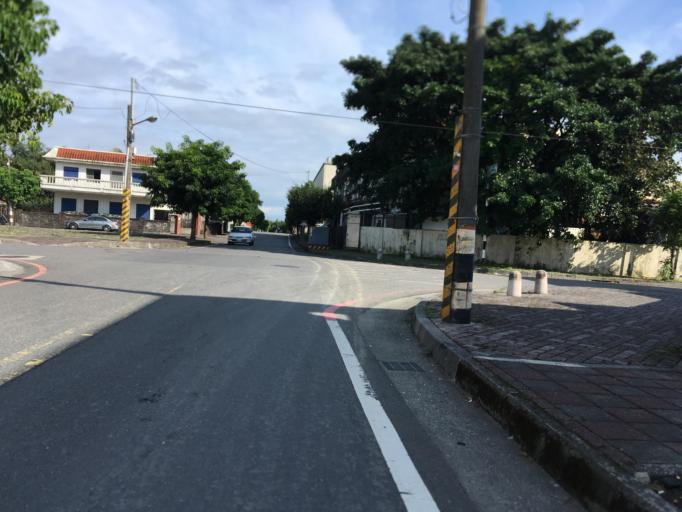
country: TW
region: Taiwan
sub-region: Yilan
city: Yilan
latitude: 24.6350
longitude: 121.8282
